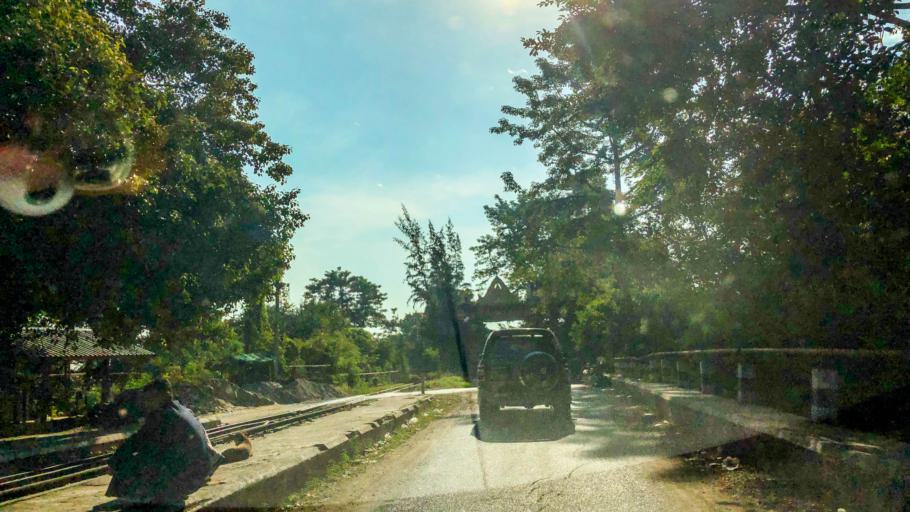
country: MM
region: Sagain
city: Sagaing
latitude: 21.8682
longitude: 95.9959
